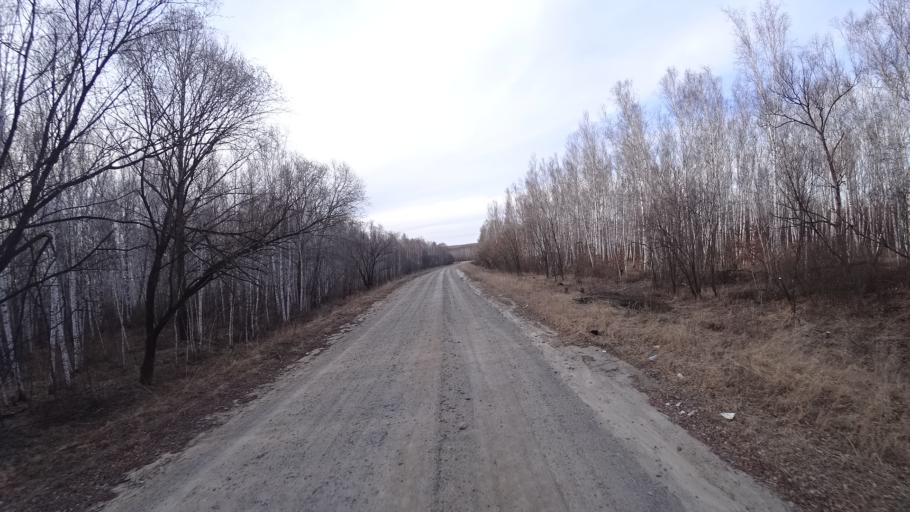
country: RU
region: Amur
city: Bureya
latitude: 50.0117
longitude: 129.7745
